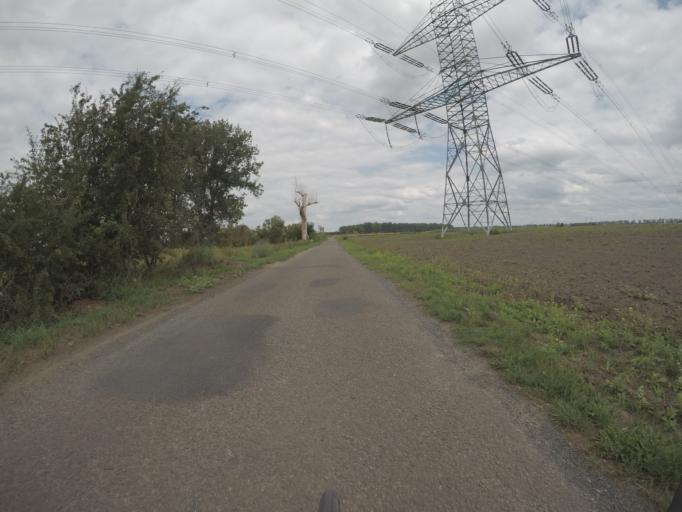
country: DE
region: Brandenburg
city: Wustermark
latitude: 52.6005
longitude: 12.9363
